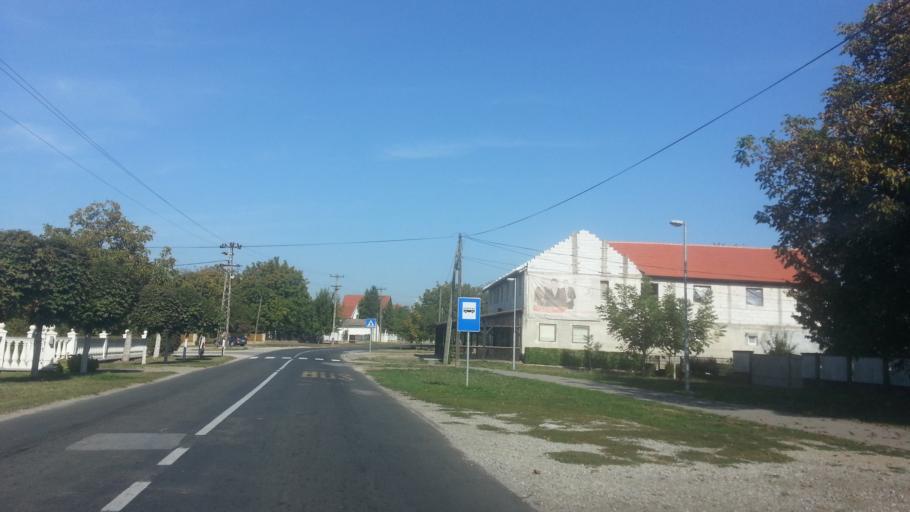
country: RS
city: Belegis
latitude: 45.0088
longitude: 20.3156
